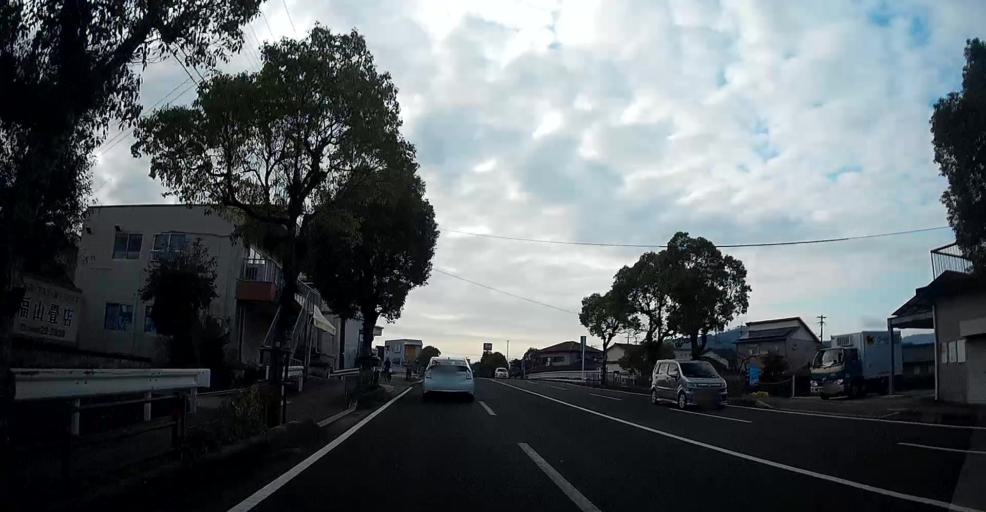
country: JP
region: Kumamoto
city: Hondo
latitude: 32.4633
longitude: 130.1906
